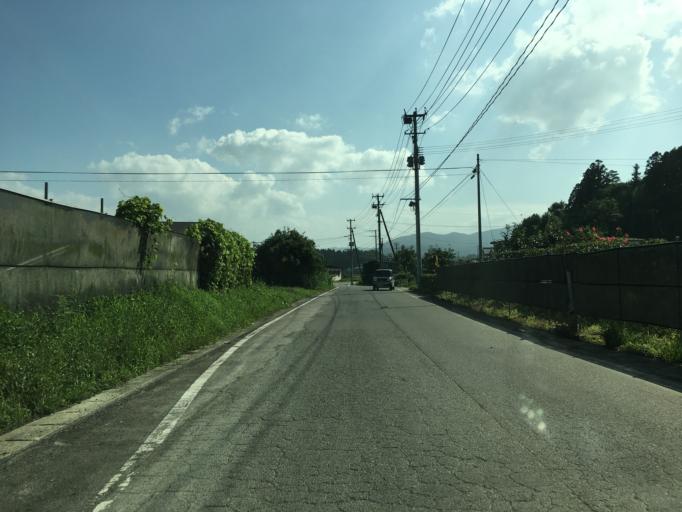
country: JP
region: Miyagi
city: Kakuda
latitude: 37.9482
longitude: 140.7774
